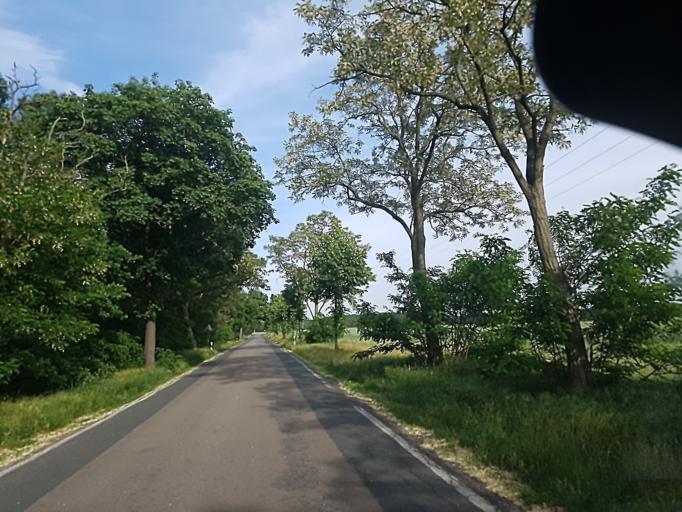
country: DE
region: Saxony-Anhalt
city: Seyda
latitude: 51.8447
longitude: 12.9102
